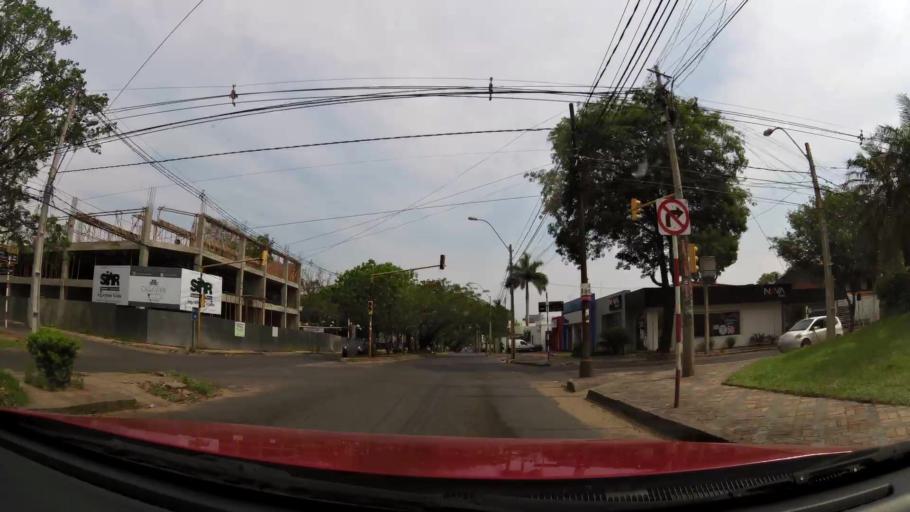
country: PY
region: Asuncion
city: Asuncion
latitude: -25.2821
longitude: -57.5712
